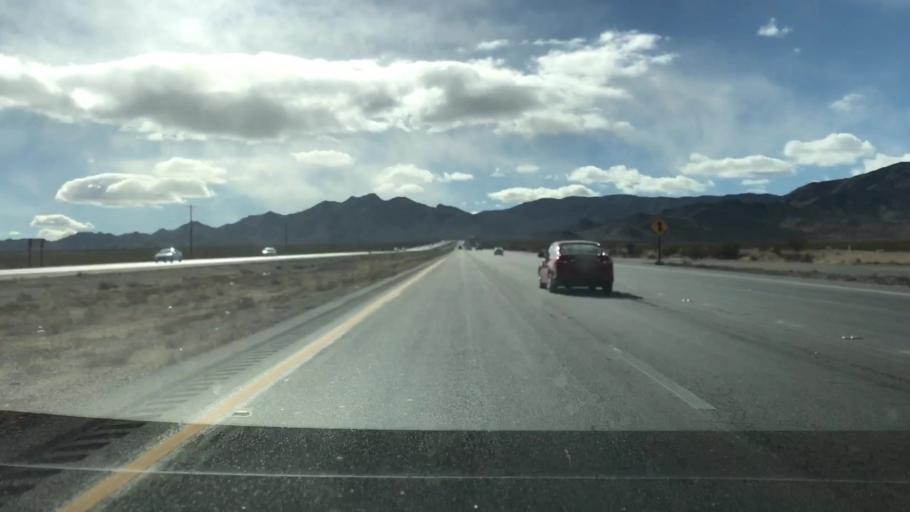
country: US
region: Nevada
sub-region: Clark County
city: Sandy Valley
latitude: 35.4959
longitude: -115.4392
